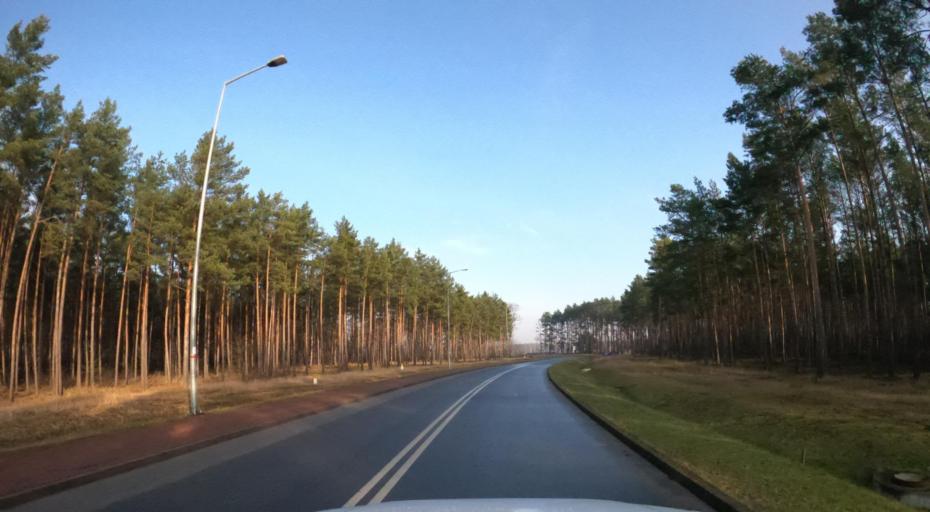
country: PL
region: Lubusz
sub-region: Powiat gorzowski
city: Kostrzyn nad Odra
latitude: 52.6243
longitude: 14.6084
